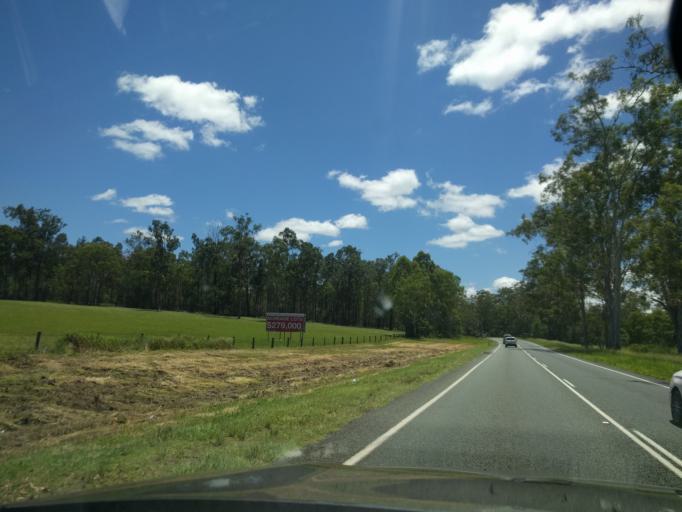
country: AU
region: Queensland
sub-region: Logan
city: Cedar Vale
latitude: -27.8496
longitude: 153.0171
